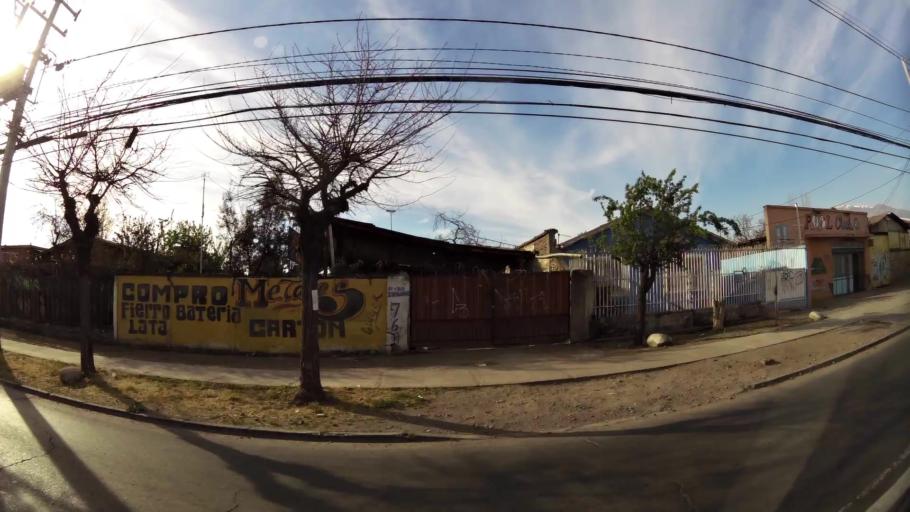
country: CL
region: Santiago Metropolitan
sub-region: Provincia de Cordillera
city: Puente Alto
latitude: -33.6133
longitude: -70.5844
